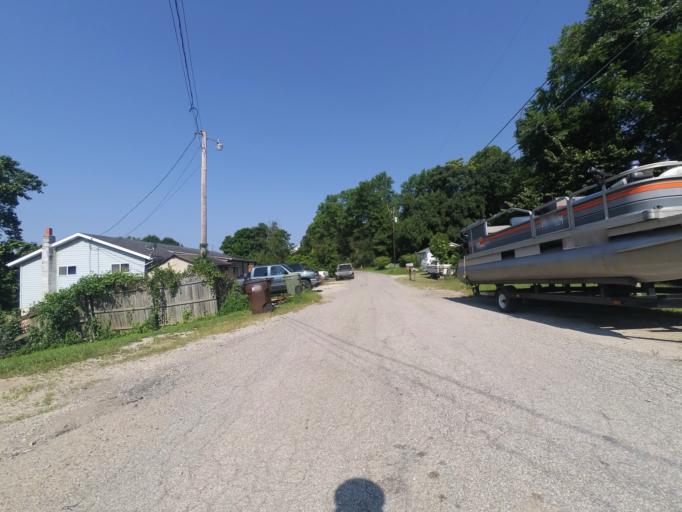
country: US
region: West Virginia
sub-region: Cabell County
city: Huntington
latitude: 38.4370
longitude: -82.4389
